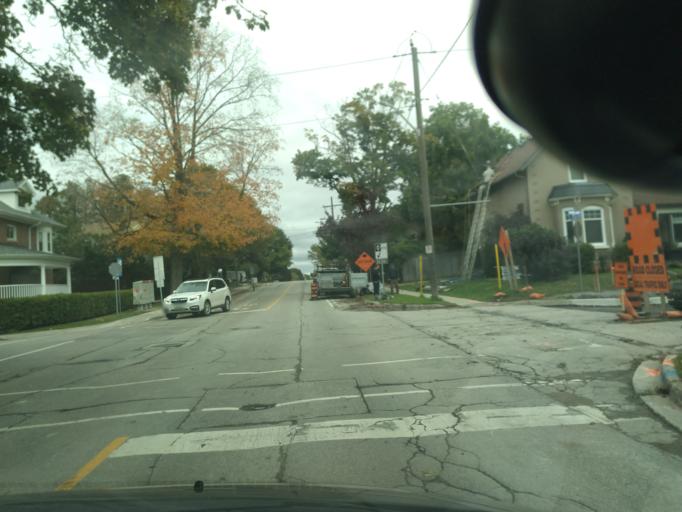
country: CA
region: Ontario
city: Newmarket
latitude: 44.0523
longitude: -79.4641
